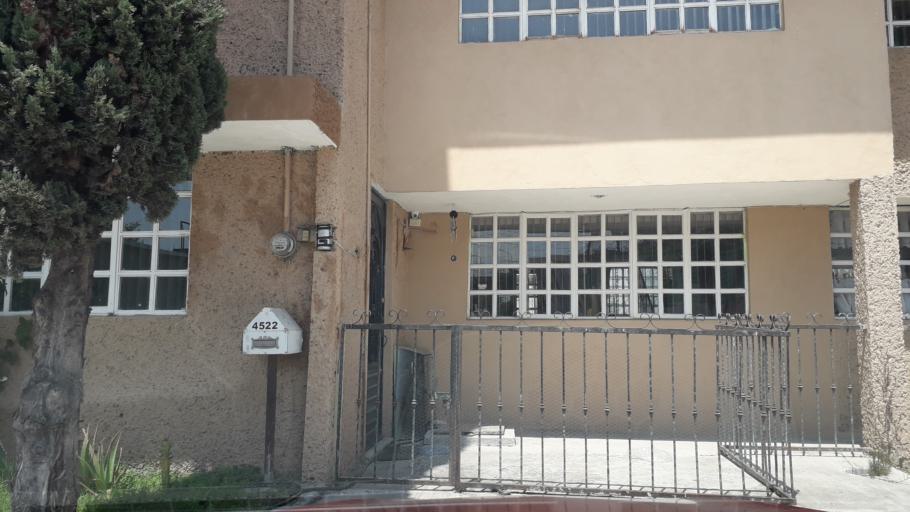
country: MX
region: Puebla
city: Puebla
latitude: 19.0541
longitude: -98.2362
